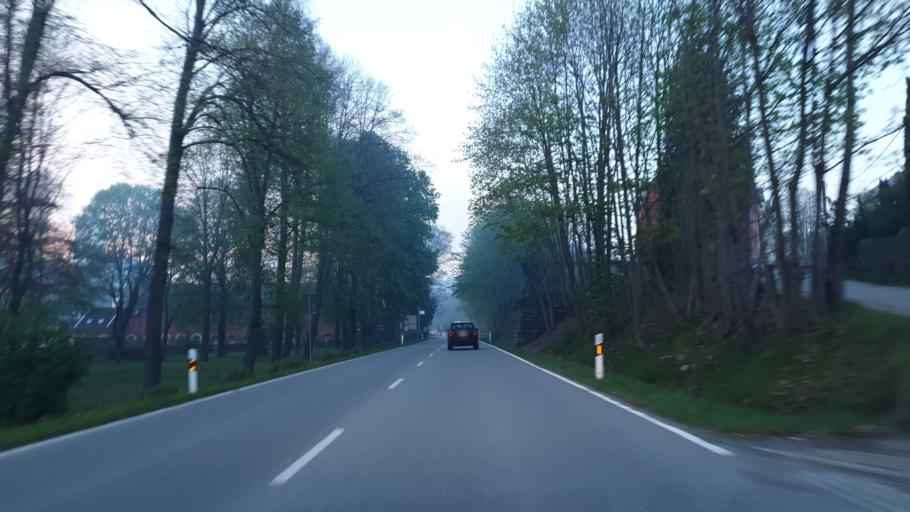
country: DE
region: Saxony
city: Lossnitz
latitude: 50.6187
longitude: 12.7320
